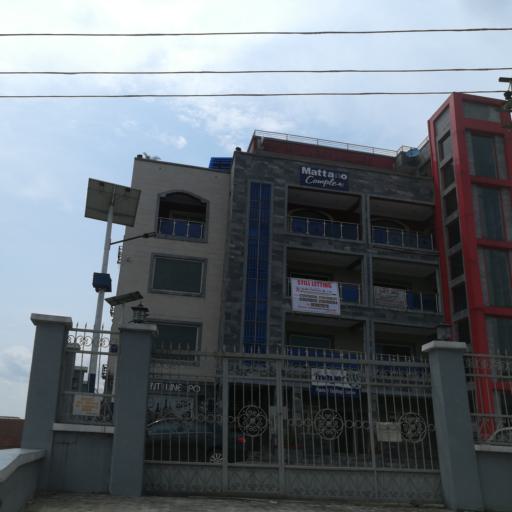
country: NG
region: Rivers
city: Port Harcourt
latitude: 4.8762
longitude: 7.0130
